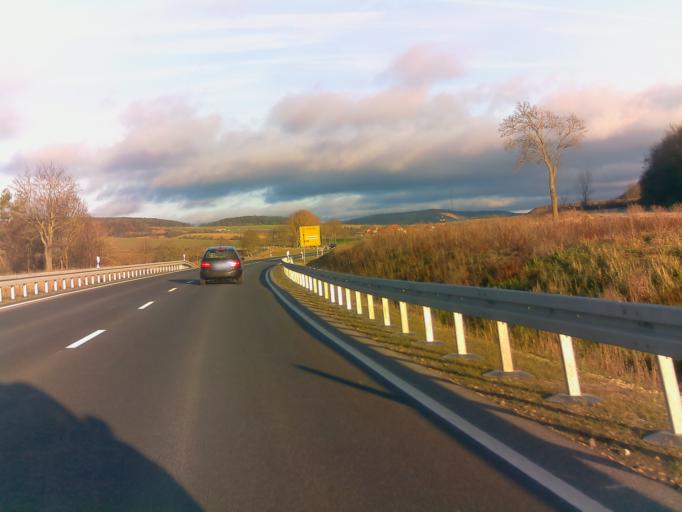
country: DE
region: Thuringia
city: Stadtilm
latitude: 50.7427
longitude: 11.0936
